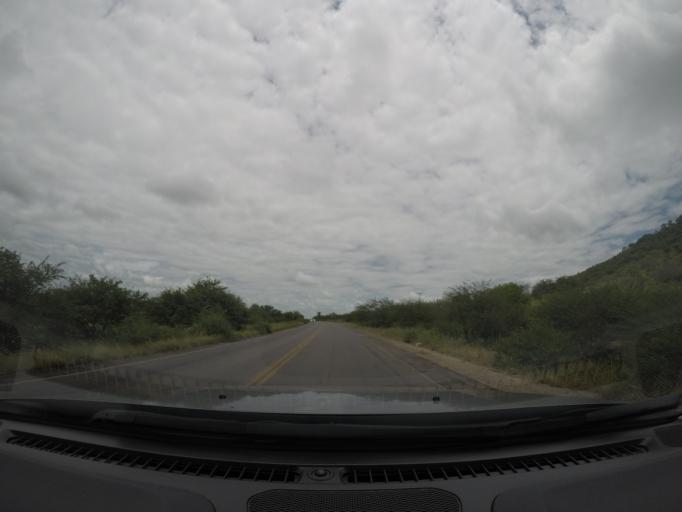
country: BR
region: Bahia
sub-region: Itaberaba
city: Itaberaba
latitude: -12.5002
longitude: -40.2447
